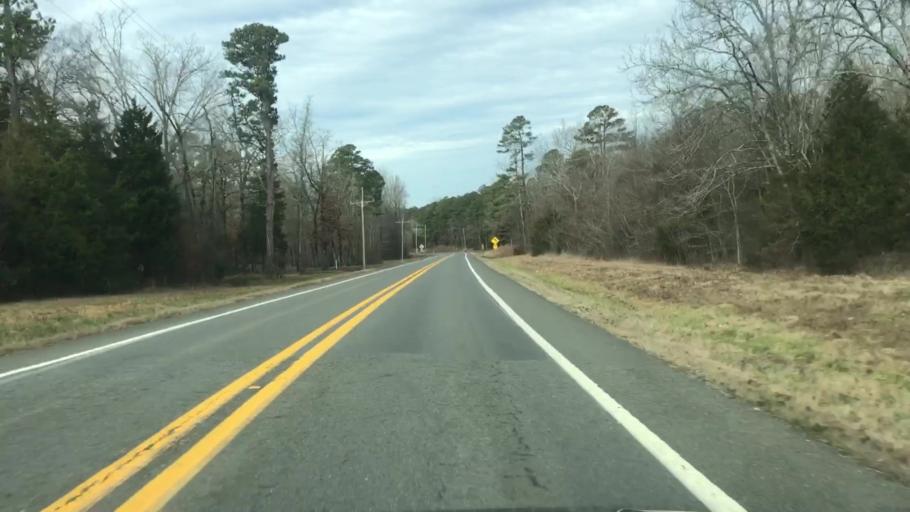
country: US
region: Arkansas
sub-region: Montgomery County
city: Mount Ida
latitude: 34.6086
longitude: -93.6841
